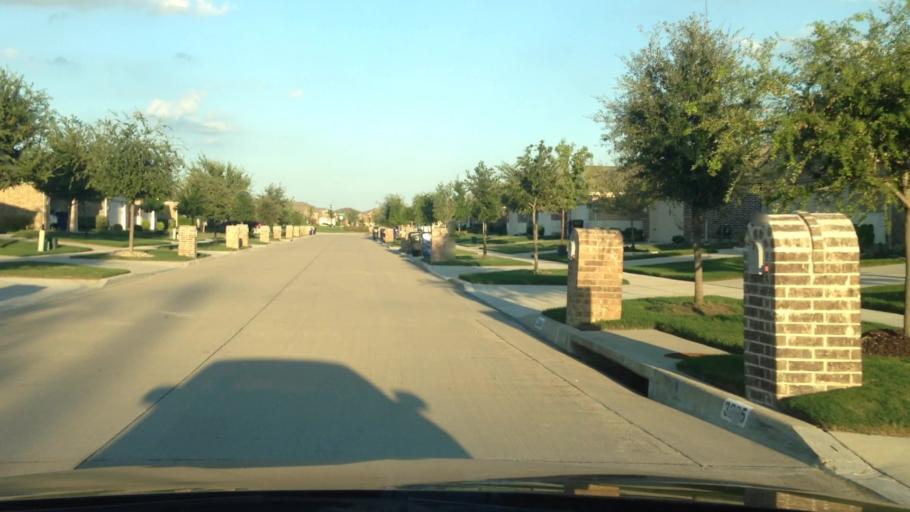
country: US
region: Texas
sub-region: Denton County
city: Little Elm
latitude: 33.1397
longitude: -96.9218
